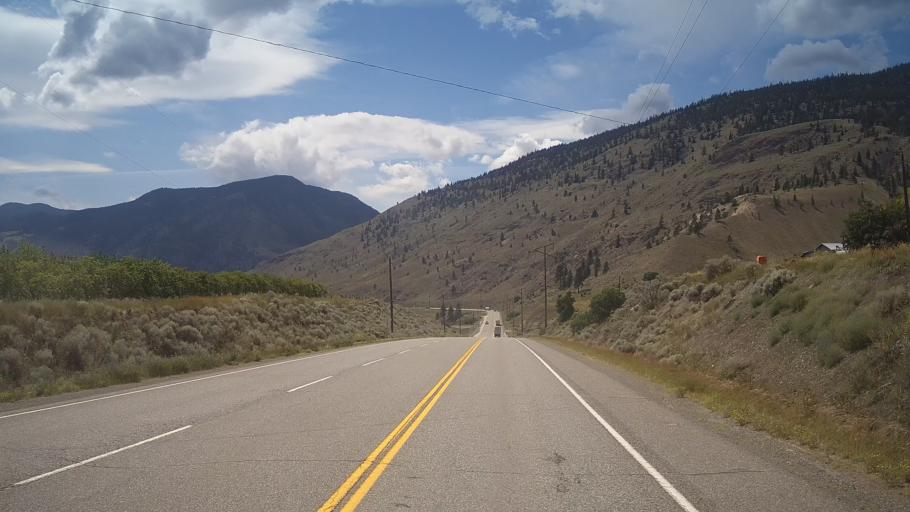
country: CA
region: British Columbia
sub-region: Thompson-Nicola Regional District
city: Ashcroft
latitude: 50.4565
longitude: -121.3053
